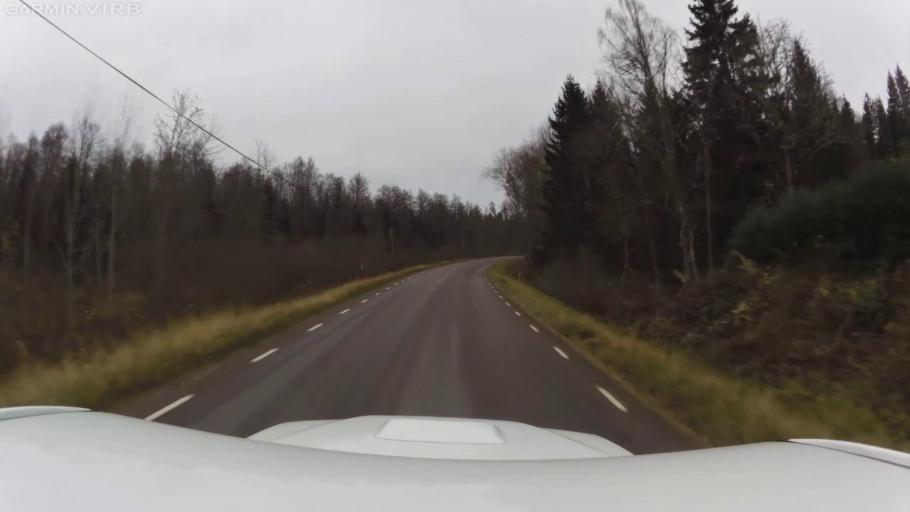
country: SE
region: OEstergoetland
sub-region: Linkopings Kommun
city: Vikingstad
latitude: 58.2449
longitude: 15.3881
